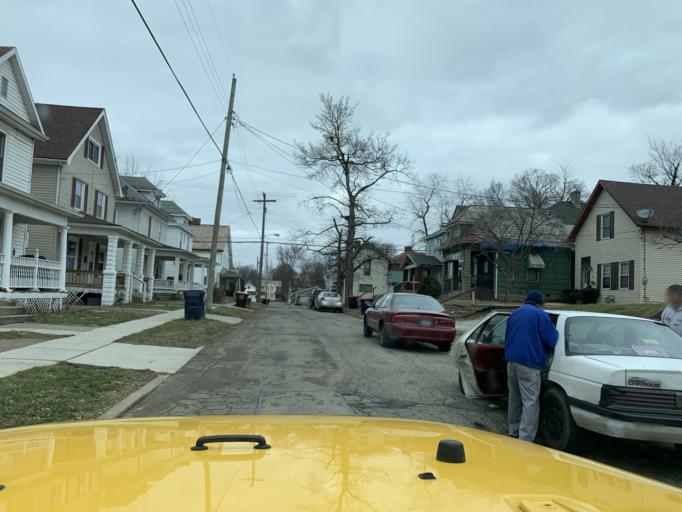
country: US
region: Ohio
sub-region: Licking County
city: Newark
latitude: 40.0578
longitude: -82.4117
